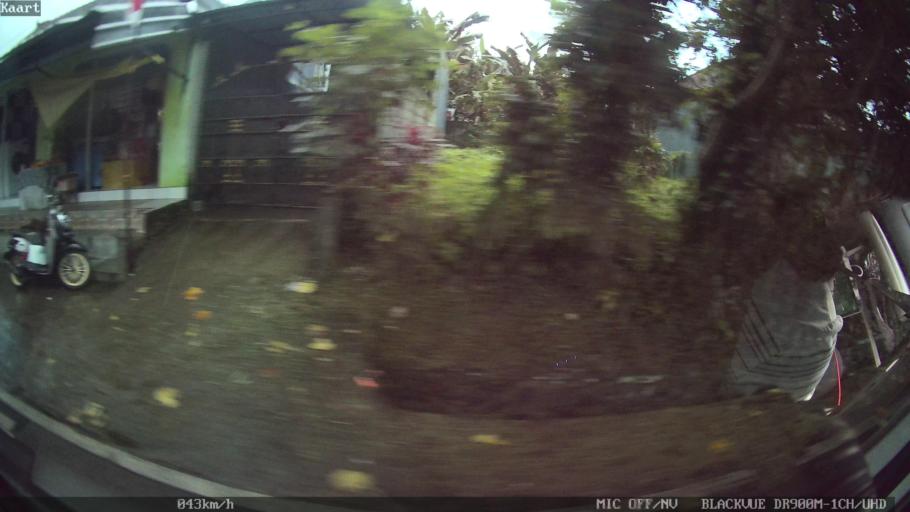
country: ID
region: Bali
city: Banjar Teguan
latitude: -8.4991
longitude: 115.2342
